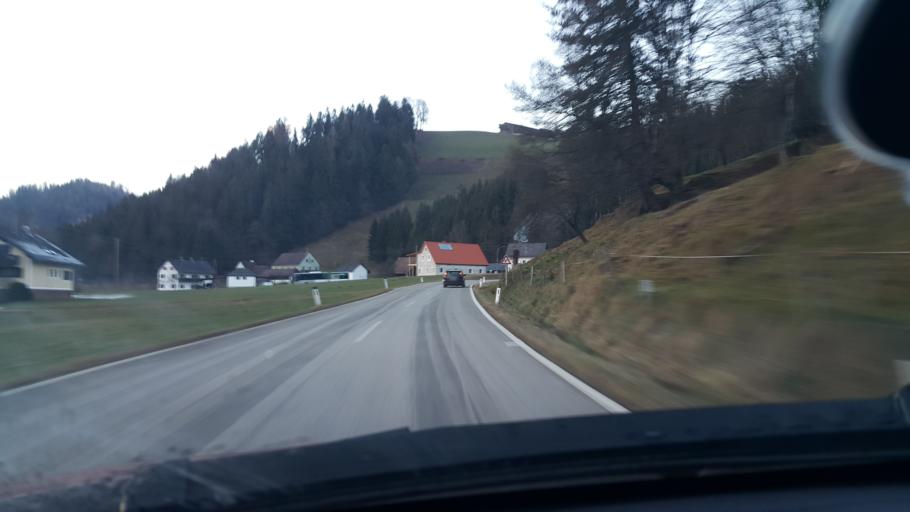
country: AT
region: Styria
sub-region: Politischer Bezirk Graz-Umgebung
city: Stiwoll
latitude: 47.1100
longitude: 15.2137
